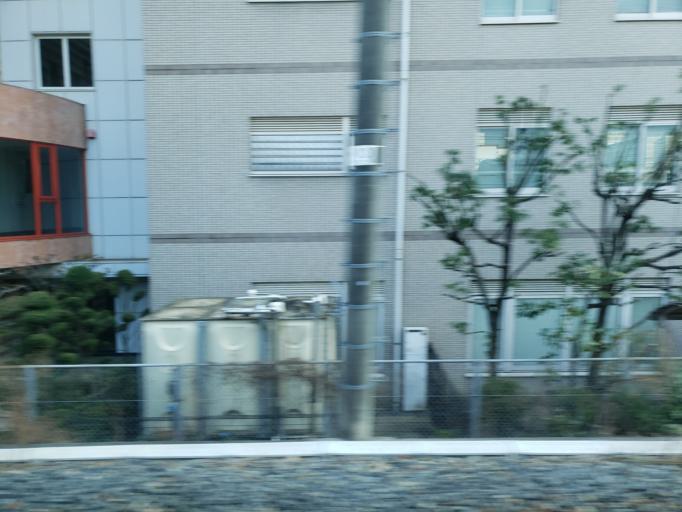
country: JP
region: Hyogo
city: Nishinomiya-hama
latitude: 34.7388
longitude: 135.3497
